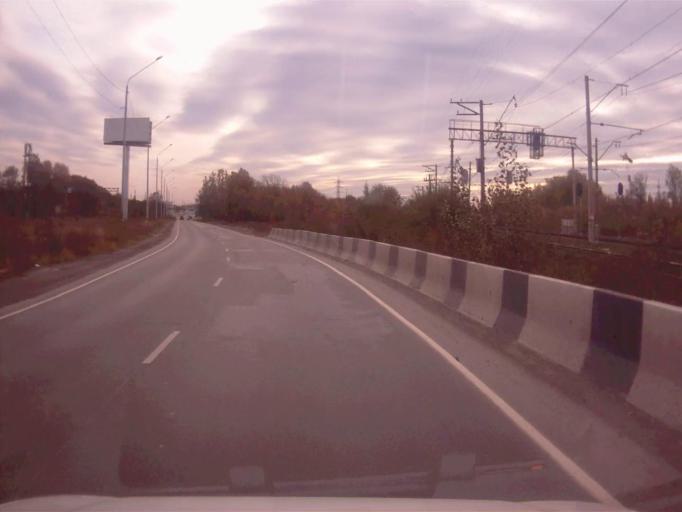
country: RU
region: Chelyabinsk
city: Novosineglazovskiy
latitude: 55.0804
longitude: 61.3879
